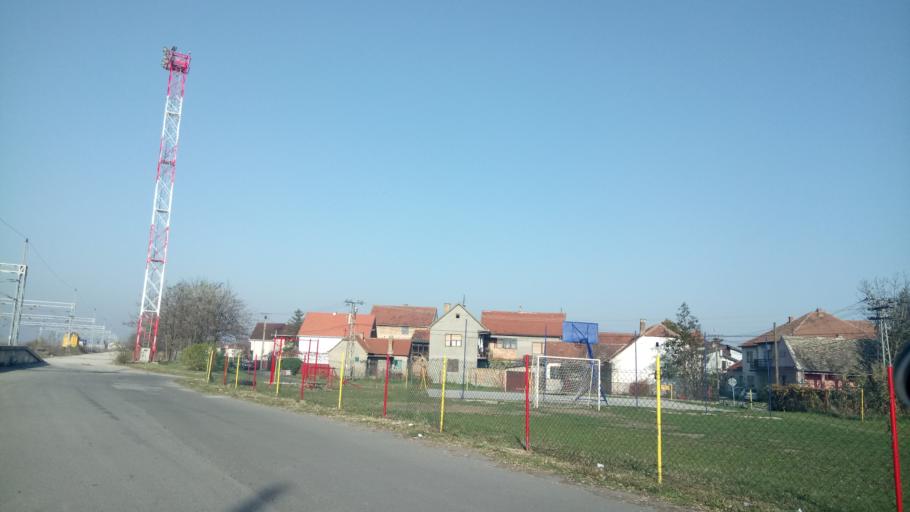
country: RS
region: Autonomna Pokrajina Vojvodina
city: Nova Pazova
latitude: 44.9383
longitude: 20.2095
